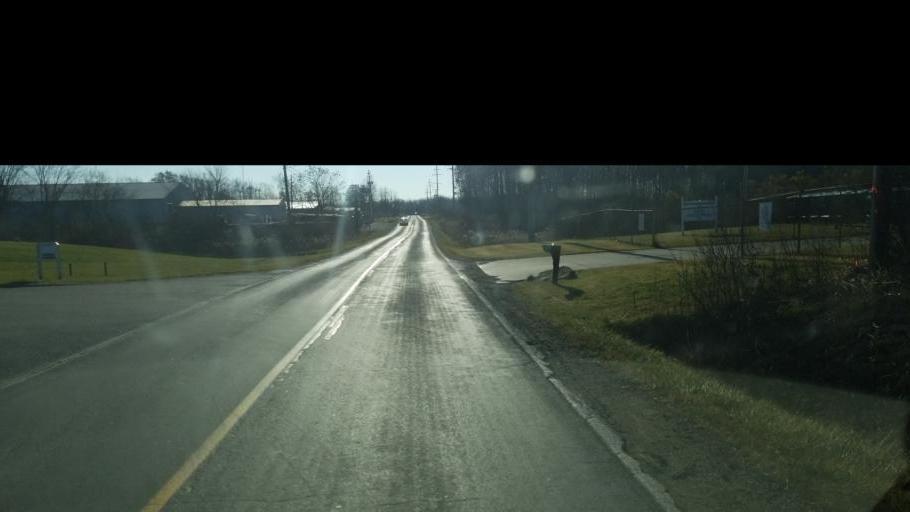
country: US
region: Ohio
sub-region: Portage County
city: Aurora
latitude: 41.3018
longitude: -81.2846
